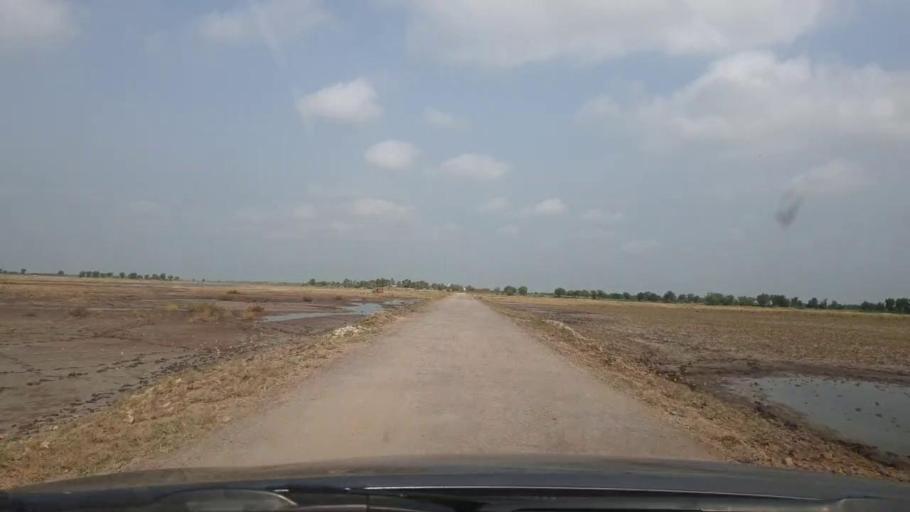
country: PK
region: Sindh
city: Ratodero
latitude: 27.8362
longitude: 68.3028
